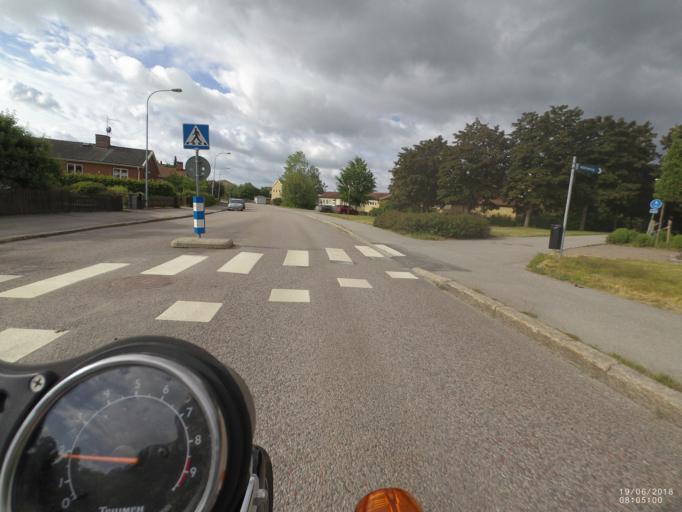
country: SE
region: Soedermanland
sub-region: Nykopings Kommun
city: Nykoping
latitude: 58.7710
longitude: 16.9792
